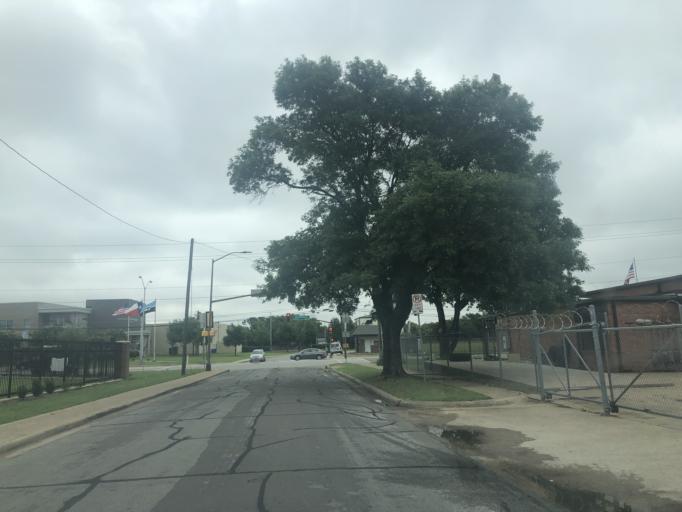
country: US
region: Texas
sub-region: Dallas County
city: Dallas
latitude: 32.7822
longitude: -96.8573
